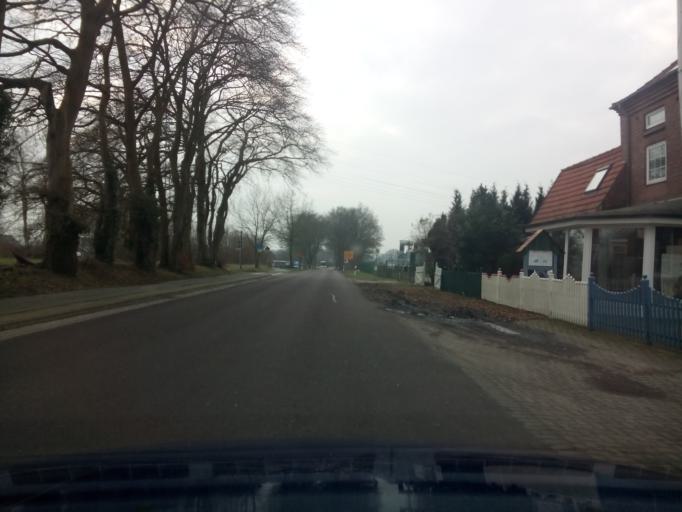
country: DE
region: Lower Saxony
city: Kuhrstedt
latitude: 53.6138
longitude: 8.8269
